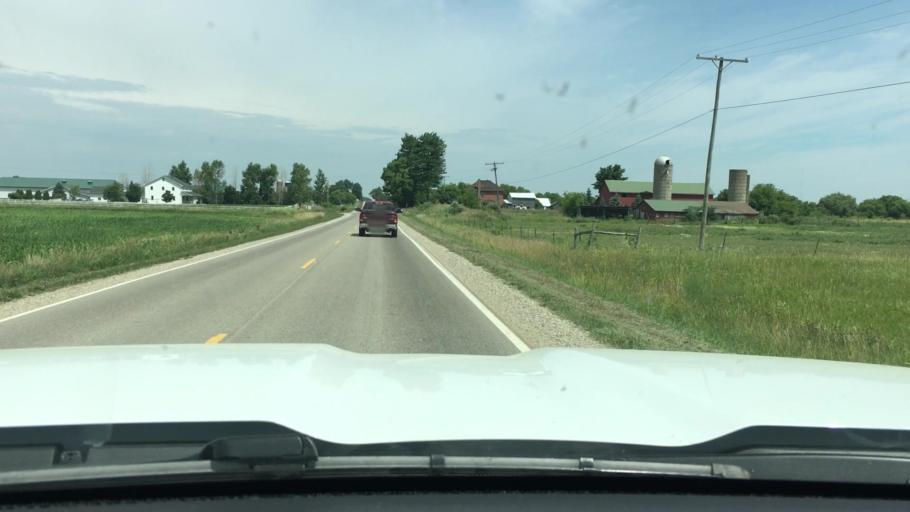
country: US
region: Michigan
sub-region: Sanilac County
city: Brown City
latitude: 43.2695
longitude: -82.9823
